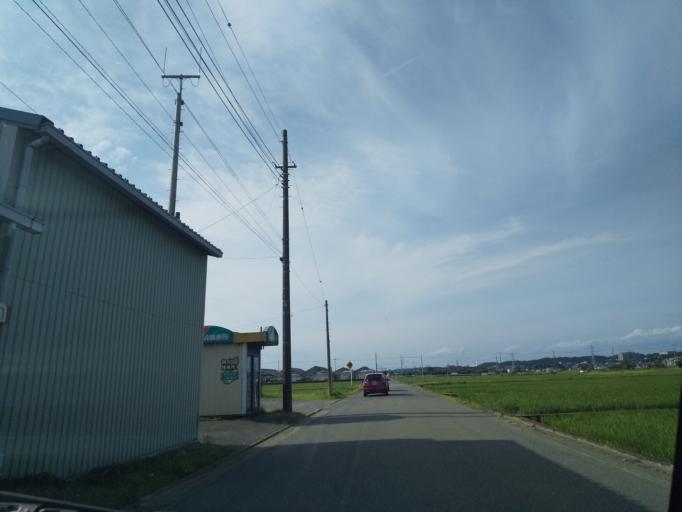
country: JP
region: Kanagawa
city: Zama
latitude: 35.4809
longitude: 139.3815
